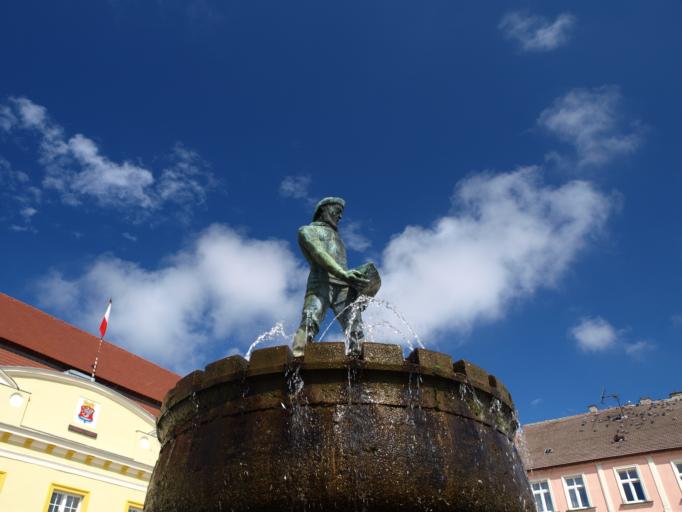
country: PL
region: West Pomeranian Voivodeship
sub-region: Powiat slawienski
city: Darlowo
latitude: 54.4222
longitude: 16.4108
